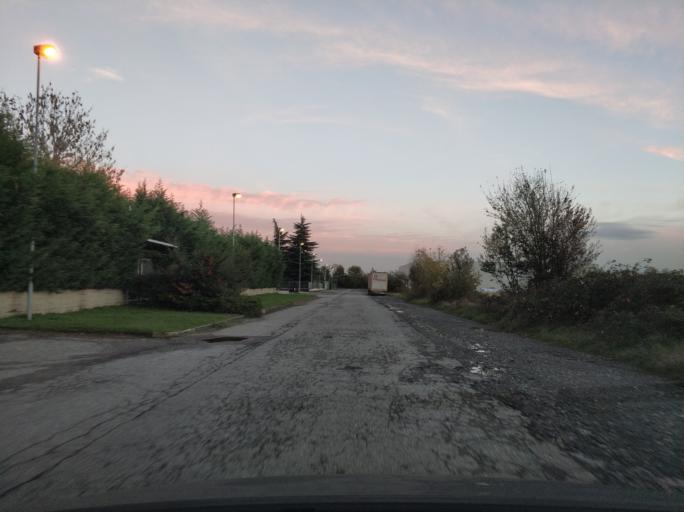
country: IT
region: Piedmont
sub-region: Provincia di Torino
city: Robassomero
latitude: 45.1777
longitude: 7.5969
